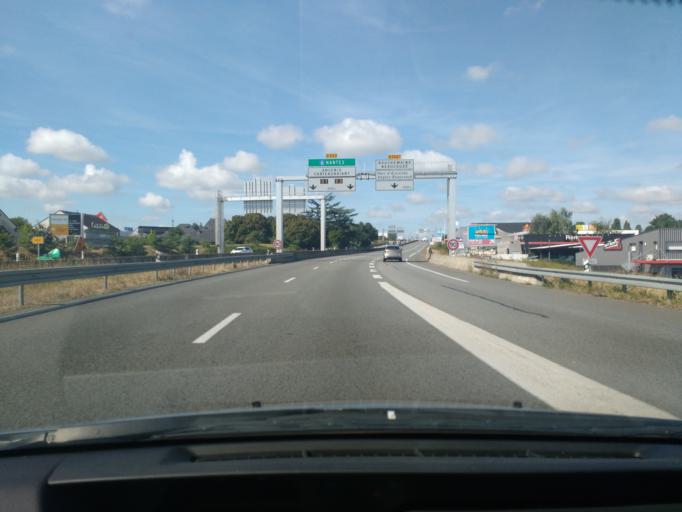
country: FR
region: Pays de la Loire
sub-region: Departement de Maine-et-Loire
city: Beaucouze
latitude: 47.4705
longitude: -0.6167
